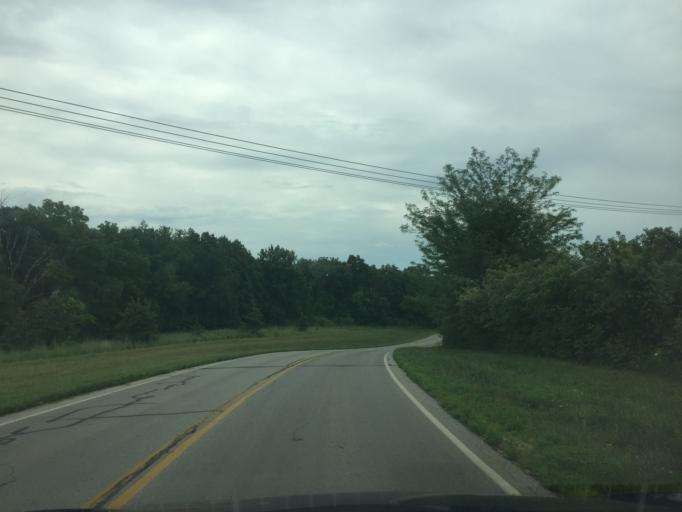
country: US
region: Missouri
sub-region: Platte County
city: Weston
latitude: 39.3694
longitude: -94.9391
